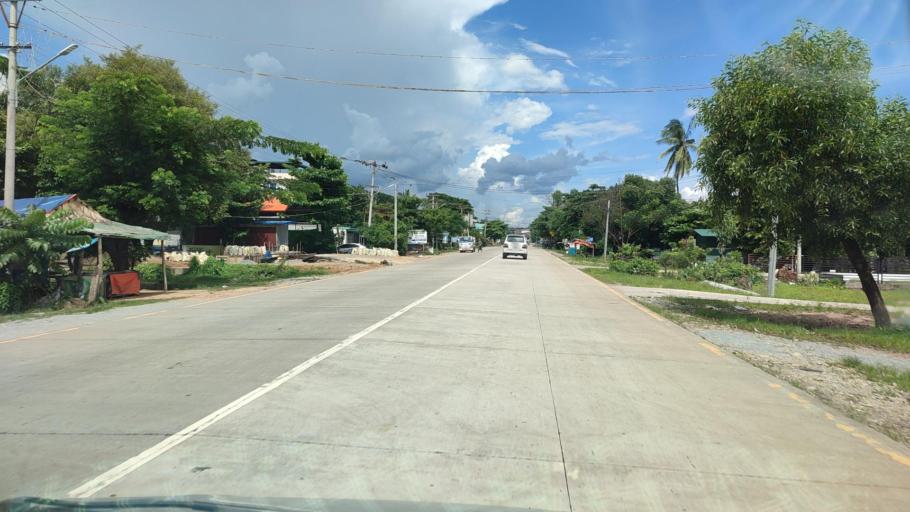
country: MM
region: Bago
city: Nyaunglebin
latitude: 17.9564
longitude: 96.7162
